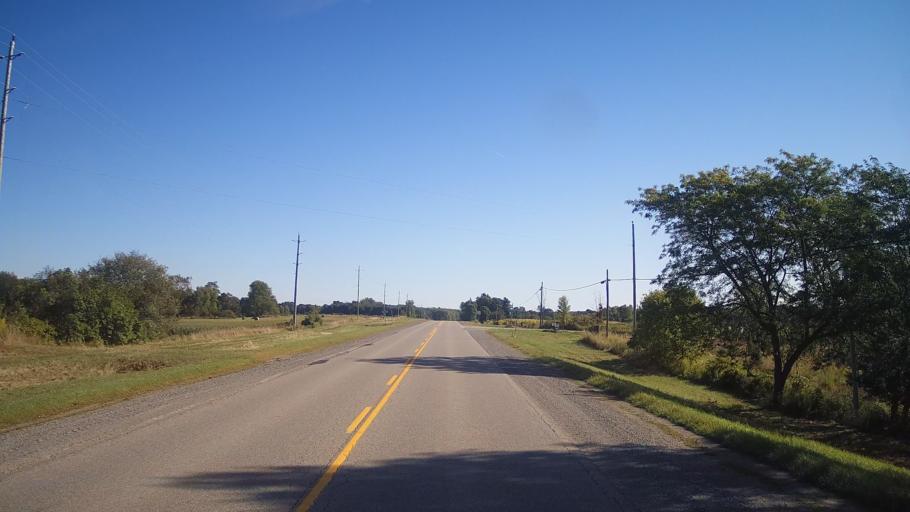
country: CA
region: Ontario
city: Gananoque
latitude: 44.5991
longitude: -76.0821
